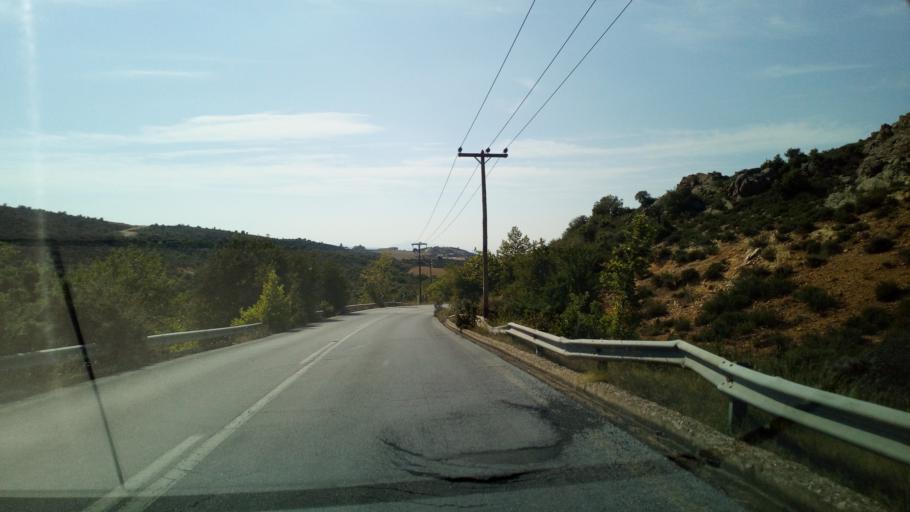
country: GR
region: Central Macedonia
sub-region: Nomos Chalkidikis
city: Arnaia
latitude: 40.5011
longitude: 23.4884
